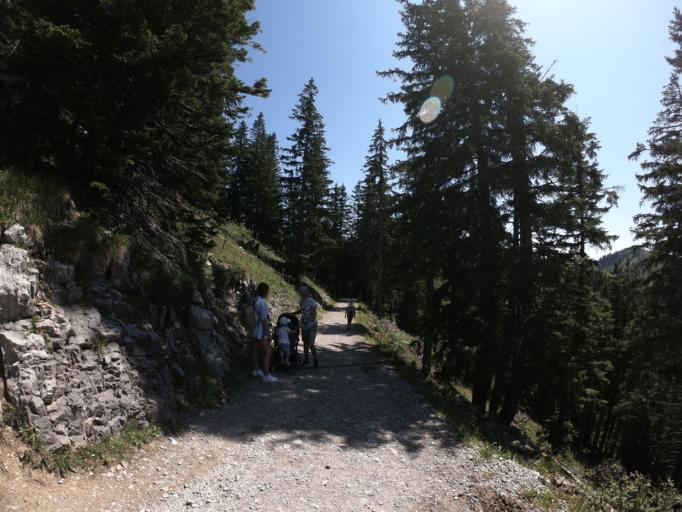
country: DE
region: Bavaria
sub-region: Upper Bavaria
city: Rottach-Egern
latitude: 47.6631
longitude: 11.7935
